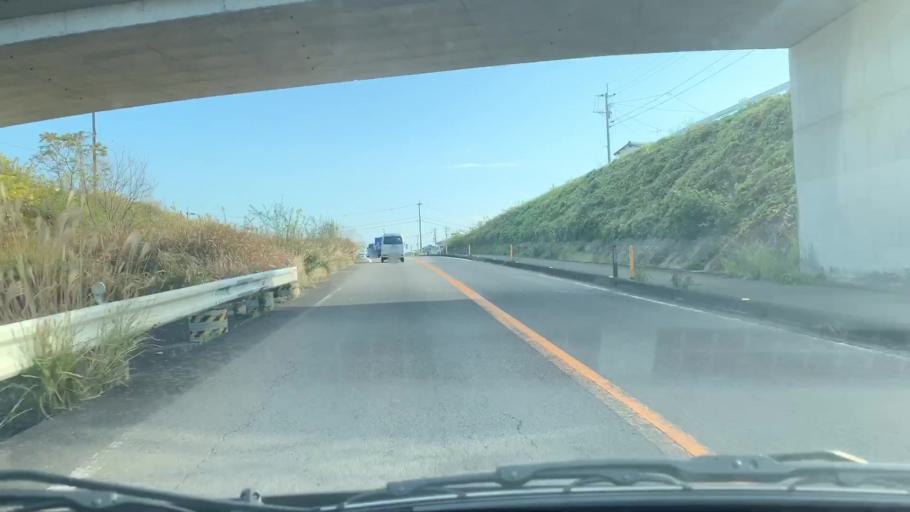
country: JP
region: Saga Prefecture
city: Kashima
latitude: 33.1008
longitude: 130.0876
